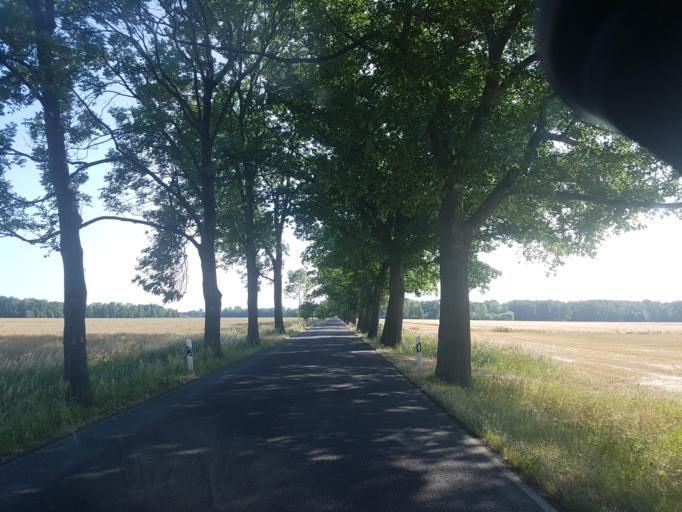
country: DE
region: Brandenburg
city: Bronkow
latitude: 51.6150
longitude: 13.9120
